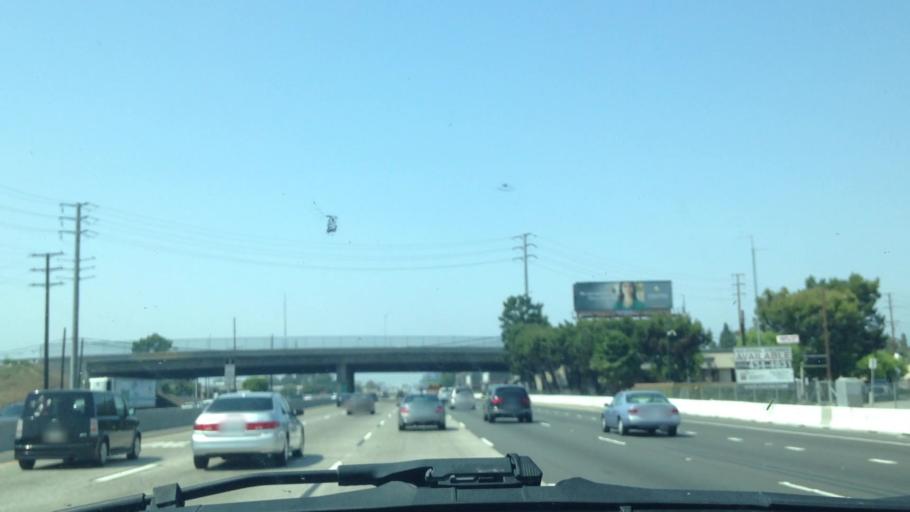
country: US
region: California
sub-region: Orange County
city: Tustin
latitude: 33.7169
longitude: -117.8436
